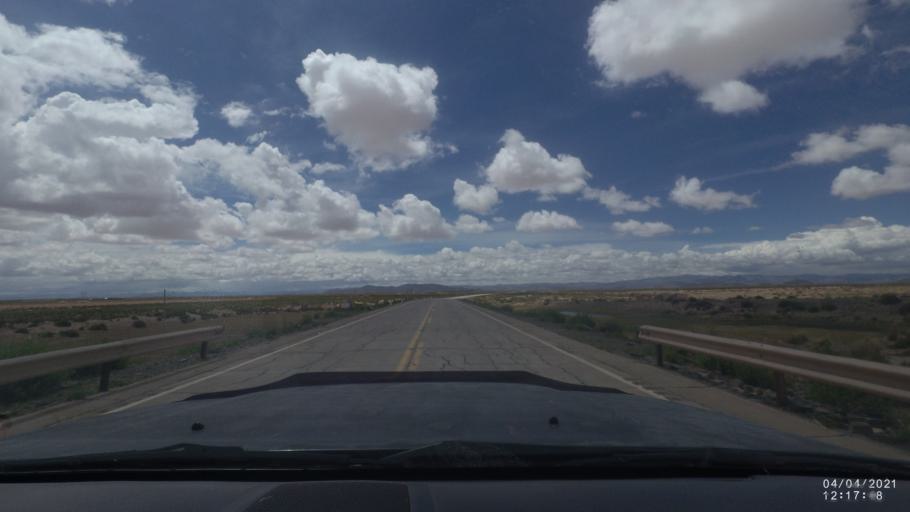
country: BO
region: Oruro
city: Oruro
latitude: -18.0964
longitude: -67.2717
